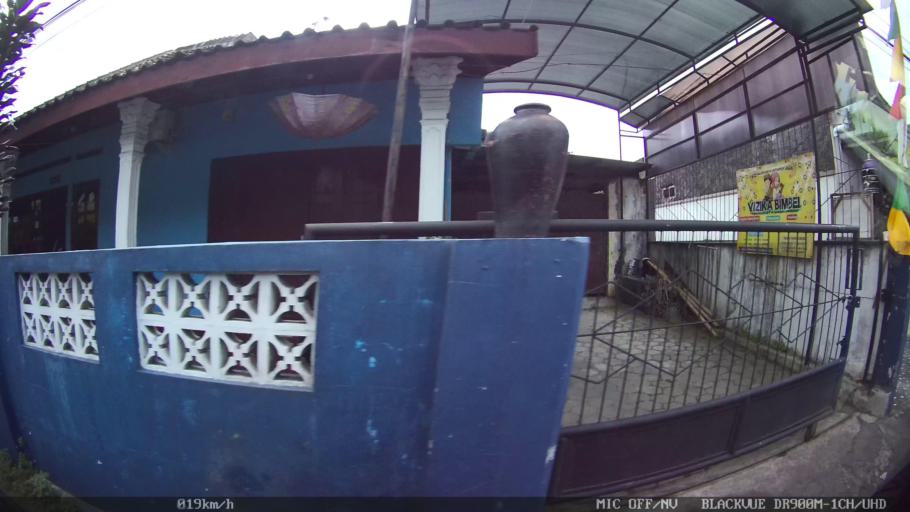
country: ID
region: Daerah Istimewa Yogyakarta
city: Yogyakarta
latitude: -7.7671
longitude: 110.3648
